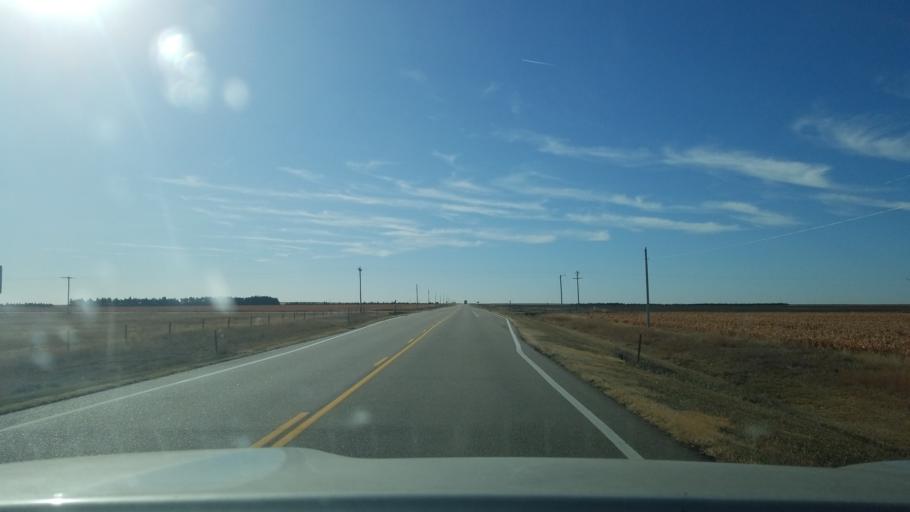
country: US
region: Kansas
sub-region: Ness County
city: Ness City
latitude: 38.3651
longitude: -99.8979
